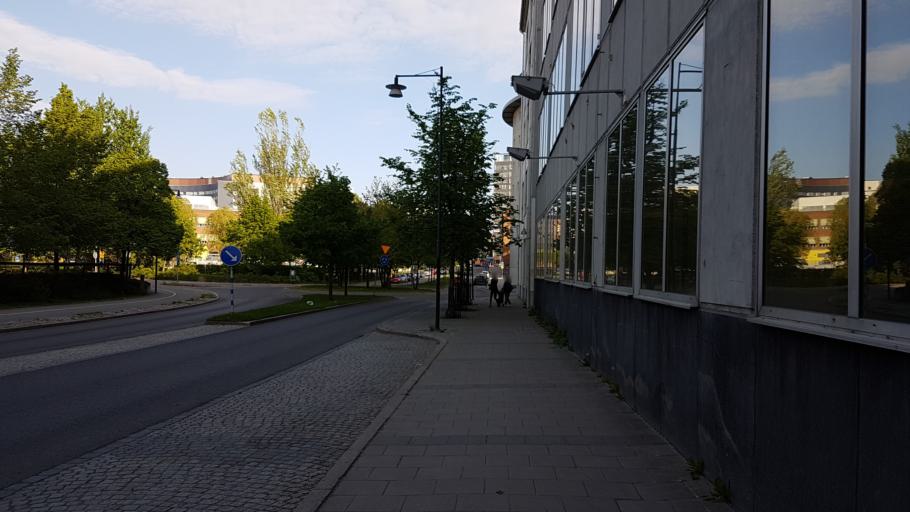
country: SE
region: Stockholm
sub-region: Sundbybergs Kommun
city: Sundbyberg
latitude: 59.3631
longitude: 17.9600
